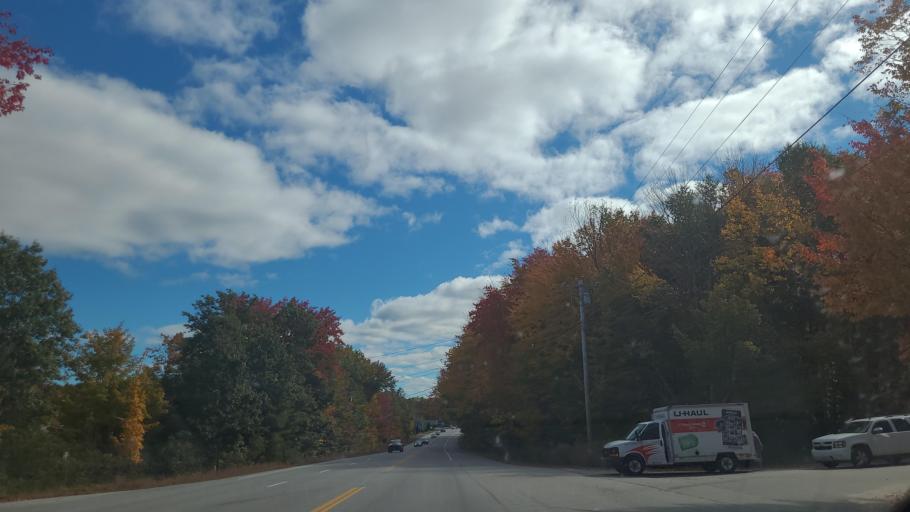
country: US
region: Maine
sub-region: Cumberland County
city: Raymond
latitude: 43.9136
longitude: -70.5171
